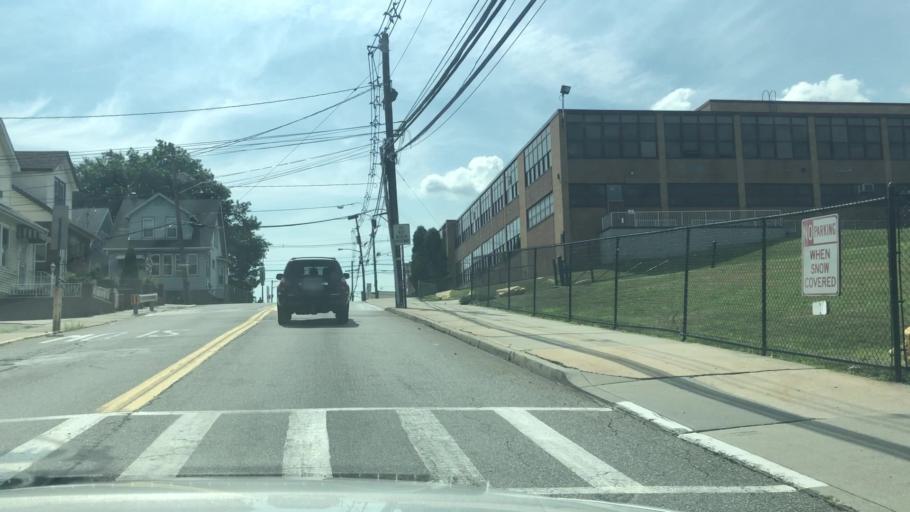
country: US
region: New Jersey
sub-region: Hudson County
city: North Bergen
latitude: 40.8029
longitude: -74.0141
